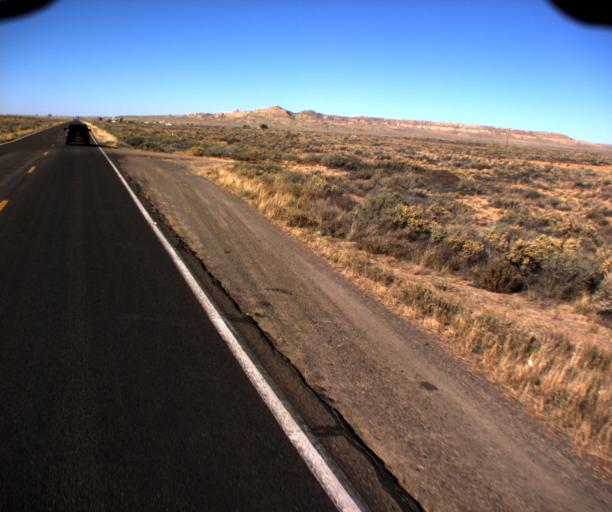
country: US
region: Arizona
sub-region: Navajo County
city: First Mesa
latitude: 35.8025
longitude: -110.4359
